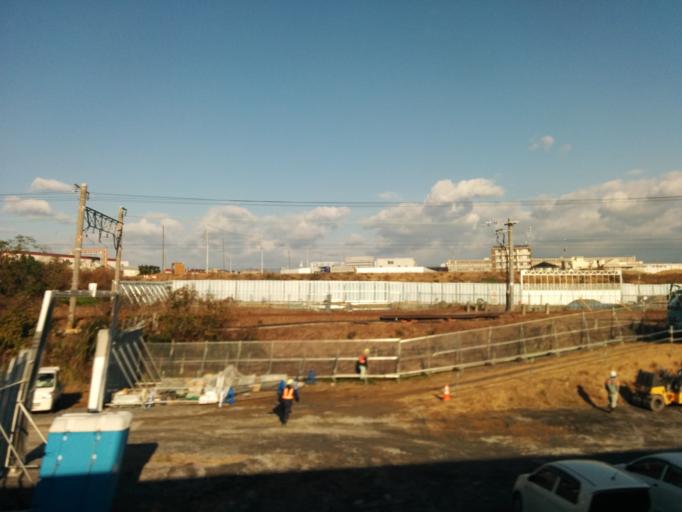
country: JP
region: Shizuoka
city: Iwata
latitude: 34.7180
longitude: 137.8853
